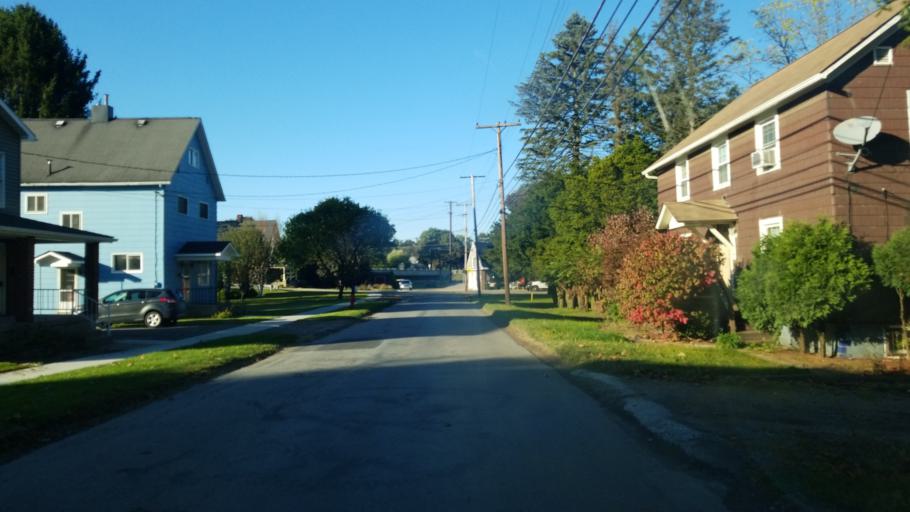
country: US
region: Pennsylvania
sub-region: Jefferson County
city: Punxsutawney
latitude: 40.9385
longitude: -78.9741
